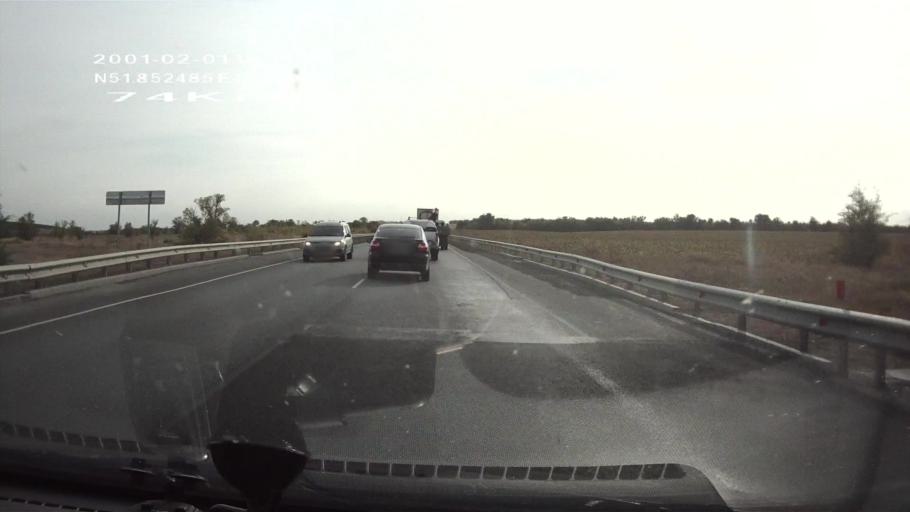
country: RU
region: Saratov
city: Yelshanka
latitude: 51.8525
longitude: 46.4906
